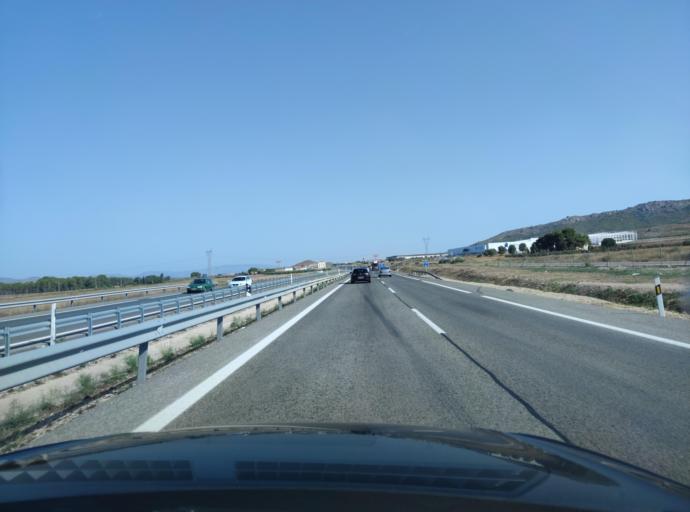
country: ES
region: Valencia
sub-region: Provincia de Alicante
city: Sax
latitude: 38.5655
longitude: -0.8341
